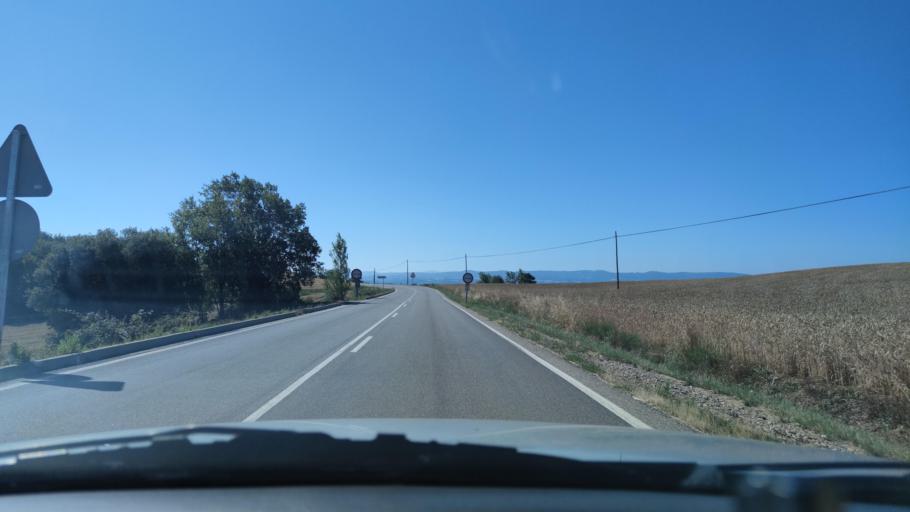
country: ES
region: Catalonia
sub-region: Provincia de Lleida
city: Solsona
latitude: 41.9152
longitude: 1.5057
